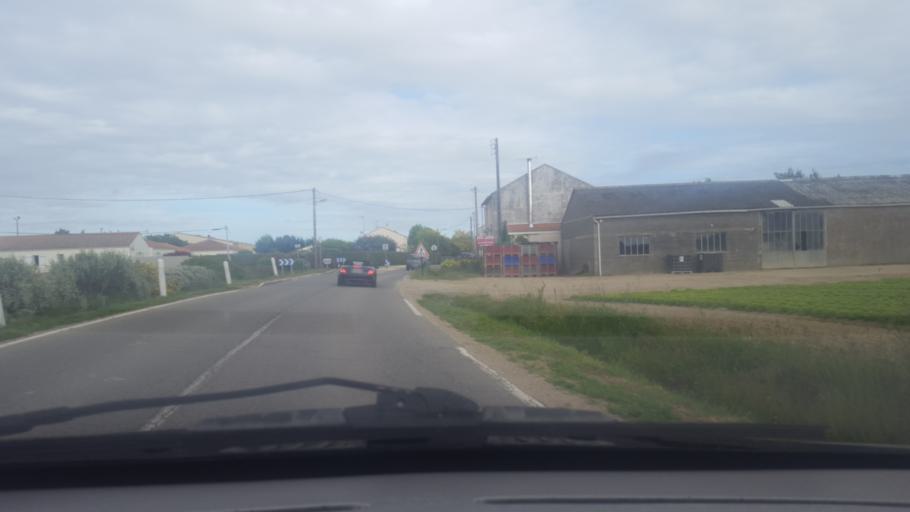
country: FR
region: Pays de la Loire
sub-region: Departement de la Loire-Atlantique
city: Machecoul
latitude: 47.0265
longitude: -1.8805
